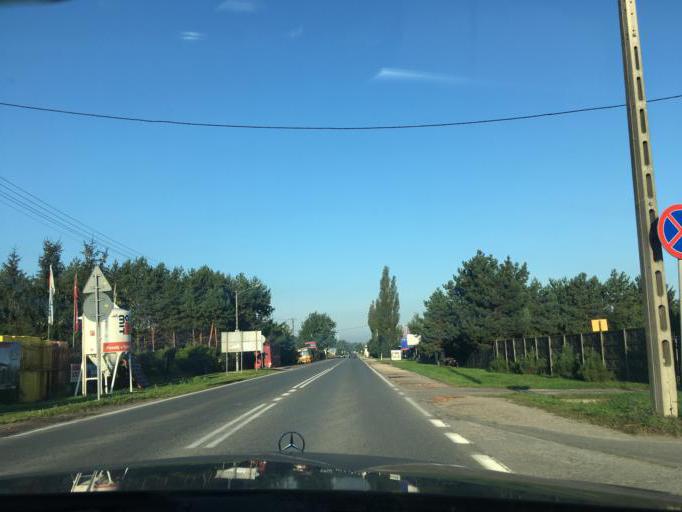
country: PL
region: Masovian Voivodeship
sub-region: Powiat pruszkowski
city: Otrebusy
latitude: 52.1310
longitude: 20.7530
